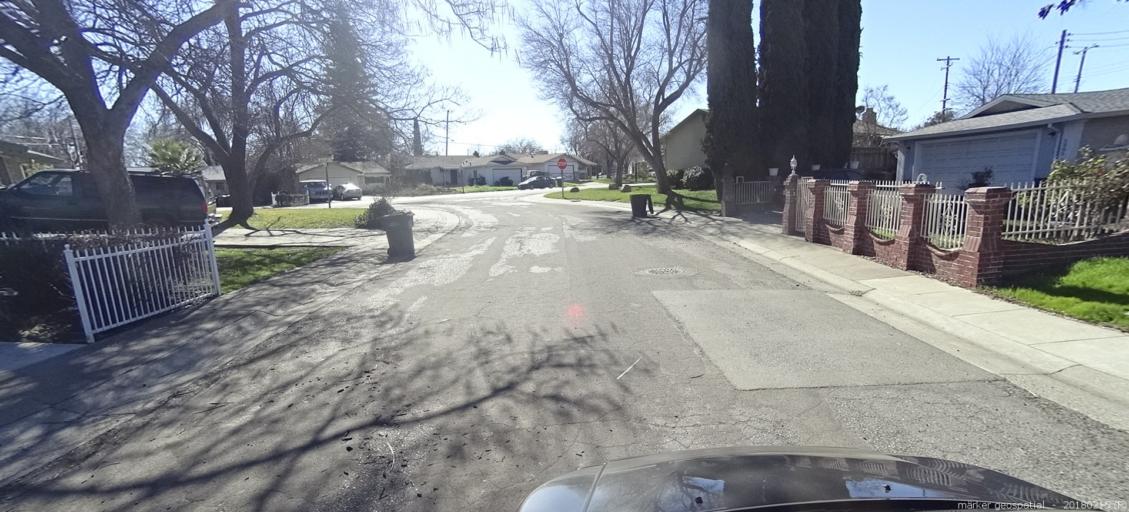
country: US
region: California
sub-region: Sacramento County
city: Foothill Farms
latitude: 38.6725
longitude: -121.3212
